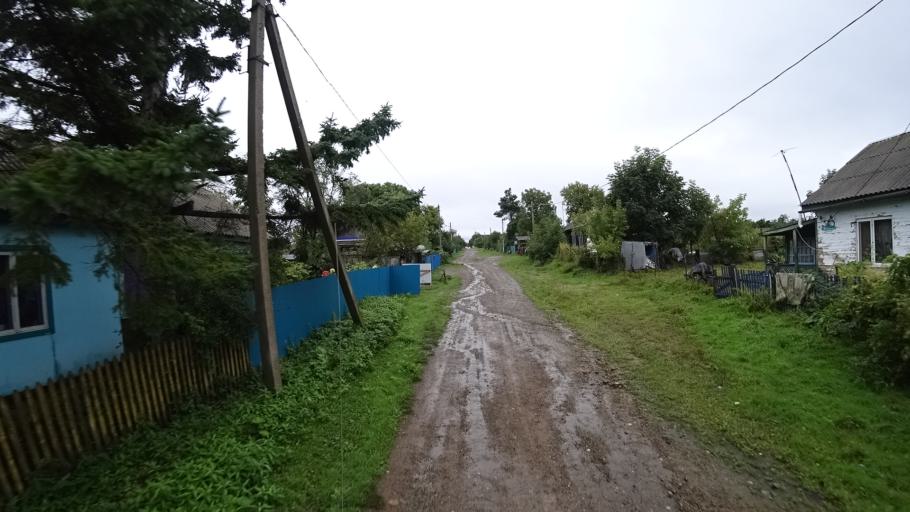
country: RU
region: Primorskiy
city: Monastyrishche
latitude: 44.2729
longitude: 132.4285
